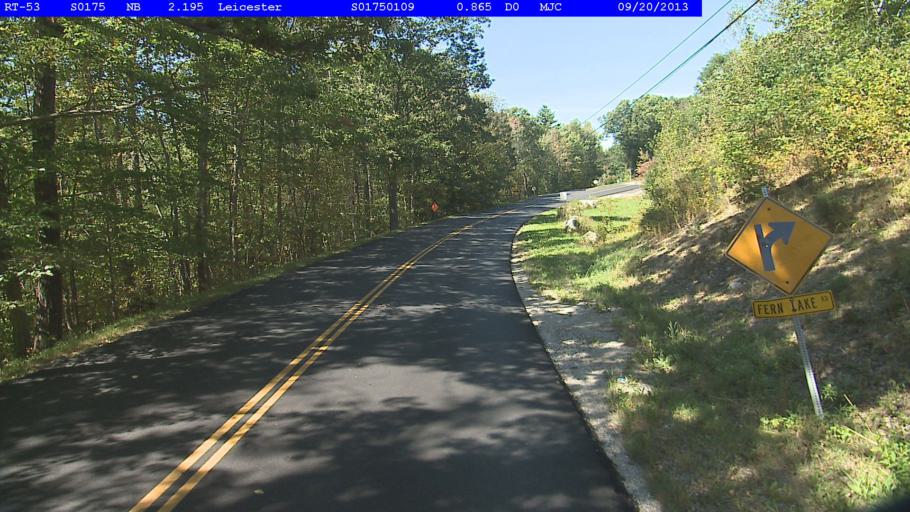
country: US
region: Vermont
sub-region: Rutland County
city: Brandon
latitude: 43.8559
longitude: -73.0665
